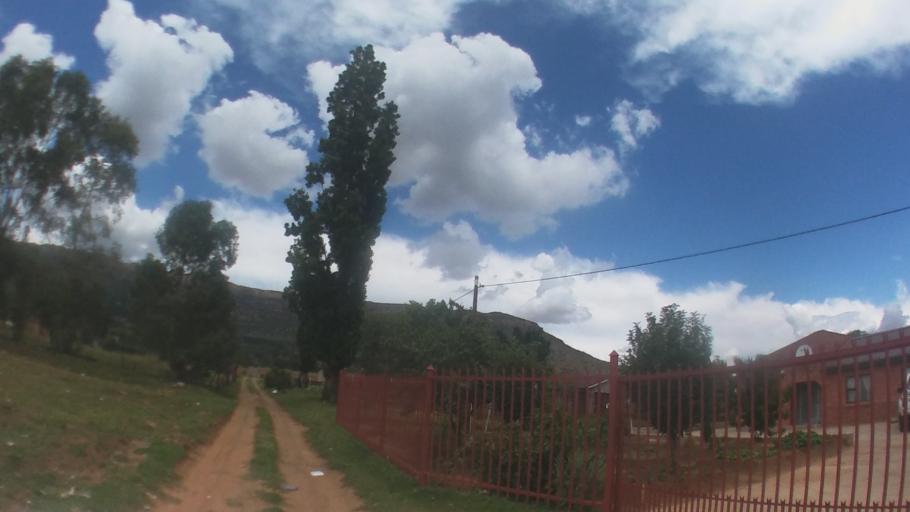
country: LS
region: Maseru
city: Nako
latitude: -29.6224
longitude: 27.5022
